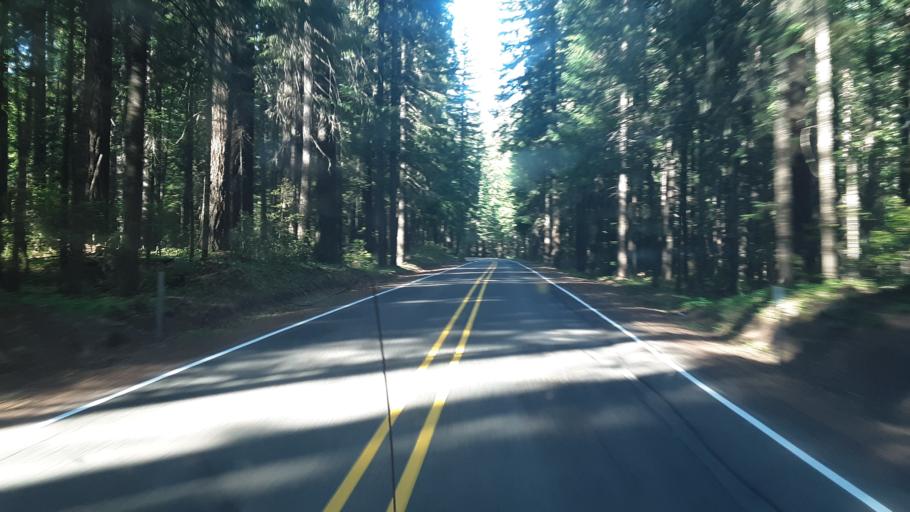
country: US
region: Oregon
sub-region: Jackson County
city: Shady Cove
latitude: 42.9433
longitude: -122.4163
